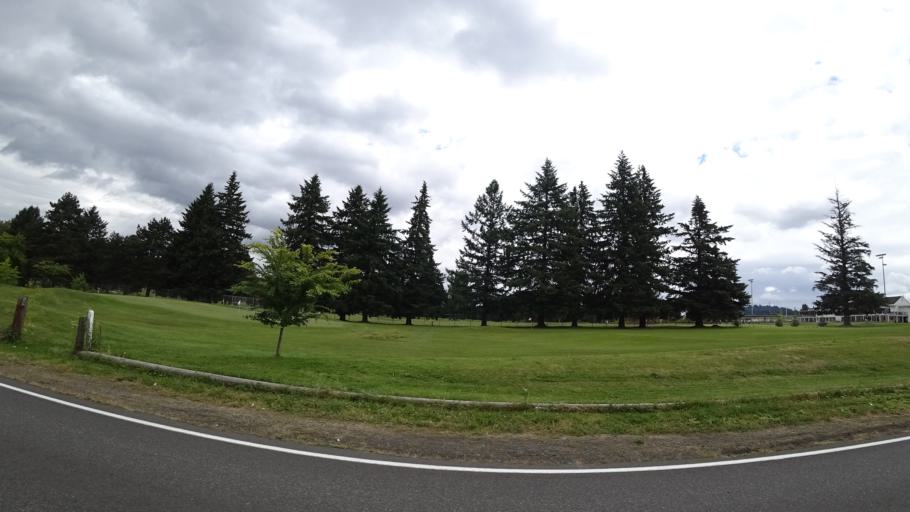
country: US
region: Oregon
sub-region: Multnomah County
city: Lents
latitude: 45.5683
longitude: -122.5882
